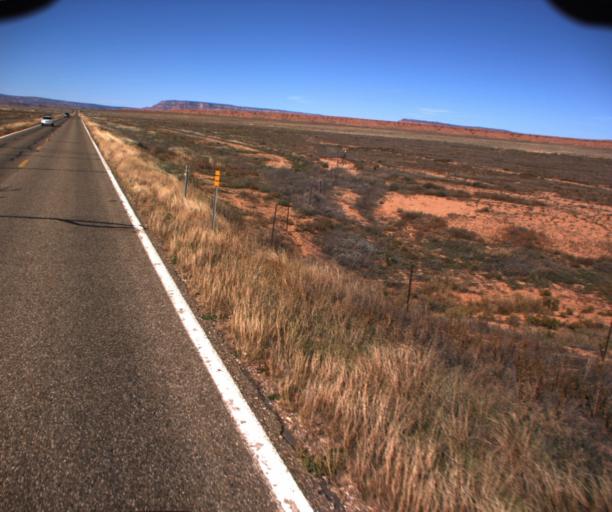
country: US
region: Arizona
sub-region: Coconino County
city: Fredonia
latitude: 36.9238
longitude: -112.4550
